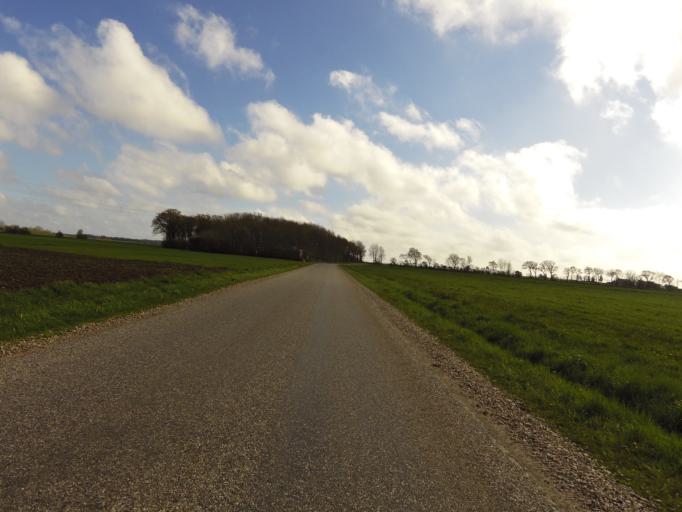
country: DK
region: South Denmark
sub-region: Vejen Kommune
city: Rodding
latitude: 55.3459
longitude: 8.9900
